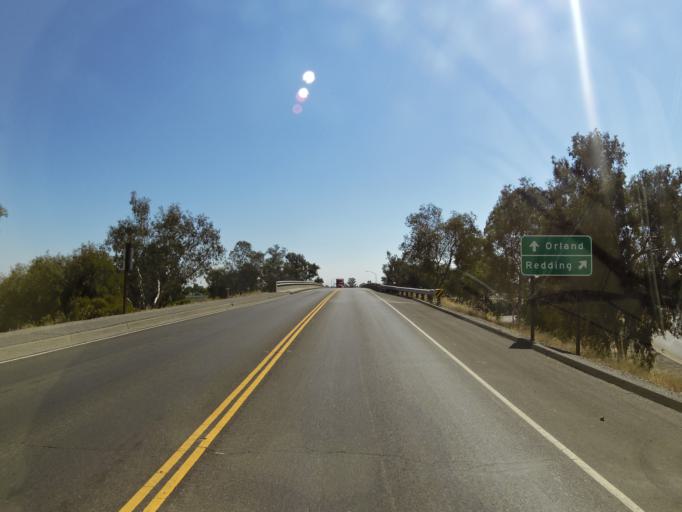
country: US
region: California
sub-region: Glenn County
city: Orland
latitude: 39.7511
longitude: -122.2066
